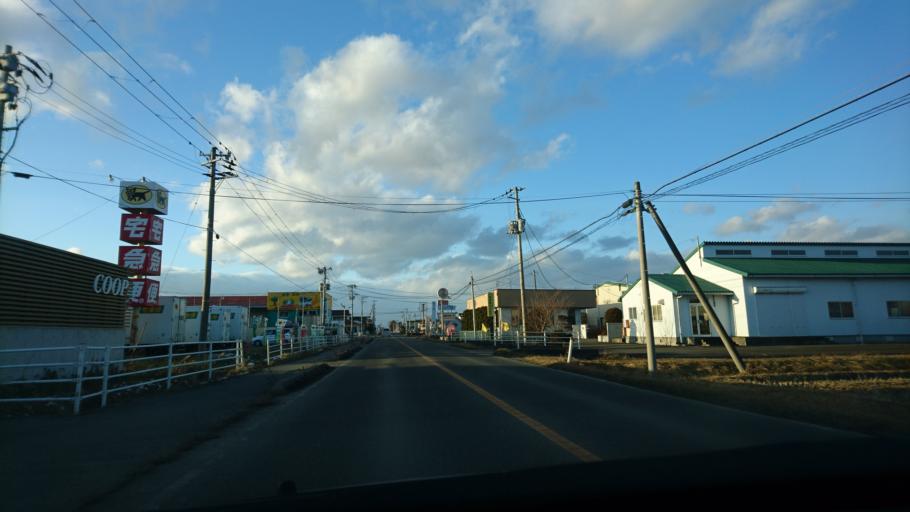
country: JP
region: Miyagi
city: Wakuya
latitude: 38.7046
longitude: 141.1847
